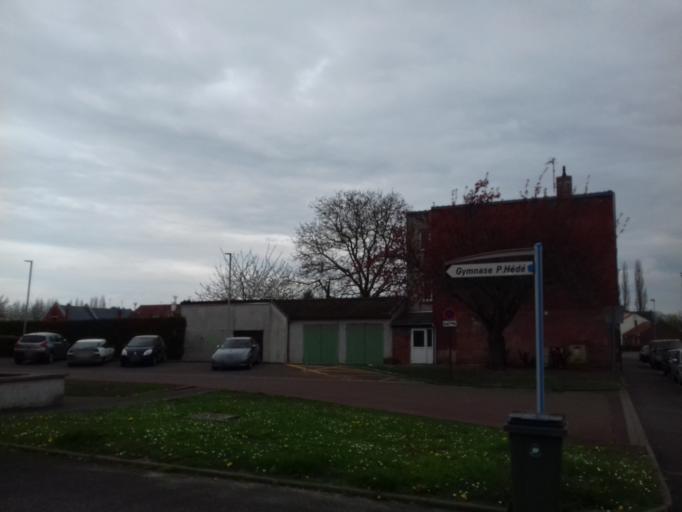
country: FR
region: Picardie
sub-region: Departement de la Somme
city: Longueau
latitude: 49.8740
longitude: 2.3556
